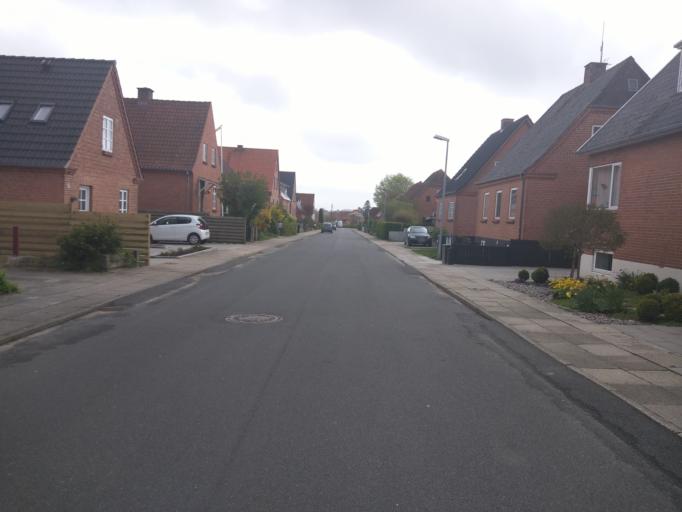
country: DK
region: Central Jutland
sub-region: Viborg Kommune
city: Viborg
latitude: 56.4560
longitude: 9.3897
